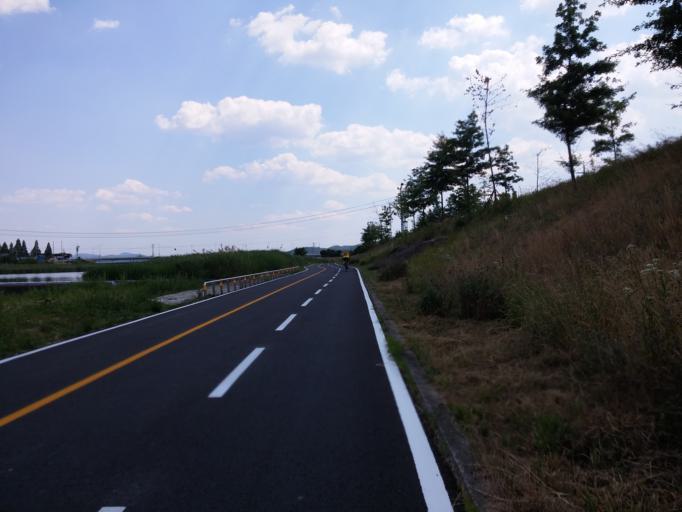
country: KR
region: Chungcheongbuk-do
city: Cheongju-si
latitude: 36.6004
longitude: 127.4975
